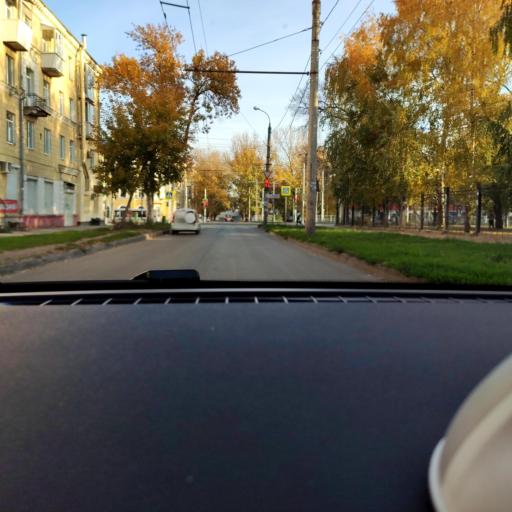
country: RU
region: Samara
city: Samara
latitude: 53.2170
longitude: 50.2550
